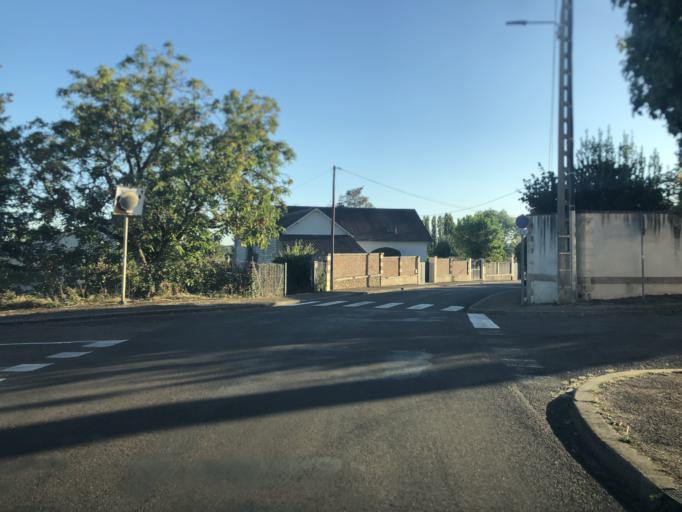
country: FR
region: Bourgogne
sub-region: Departement de l'Yonne
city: Joigny
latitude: 47.9809
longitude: 3.4064
